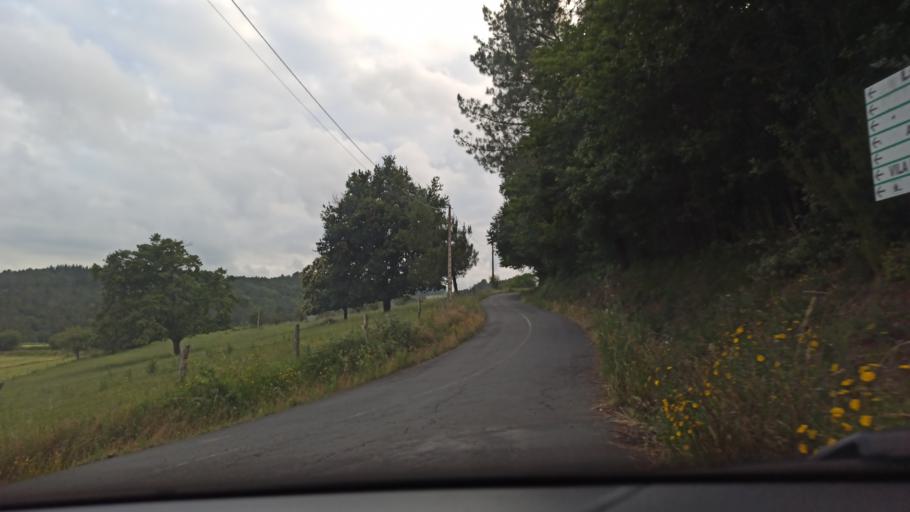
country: ES
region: Galicia
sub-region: Provincia da Coruna
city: Santiso
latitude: 42.8200
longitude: -8.1421
